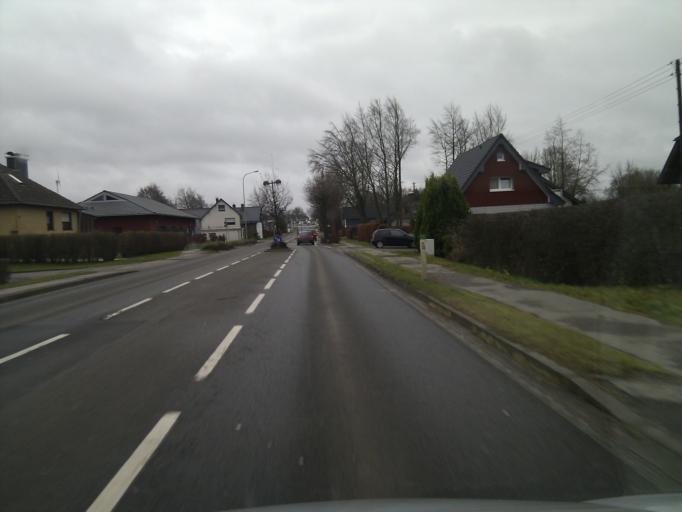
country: DE
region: North Rhine-Westphalia
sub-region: Regierungsbezirk Koln
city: Monschau
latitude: 50.5835
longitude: 6.2573
